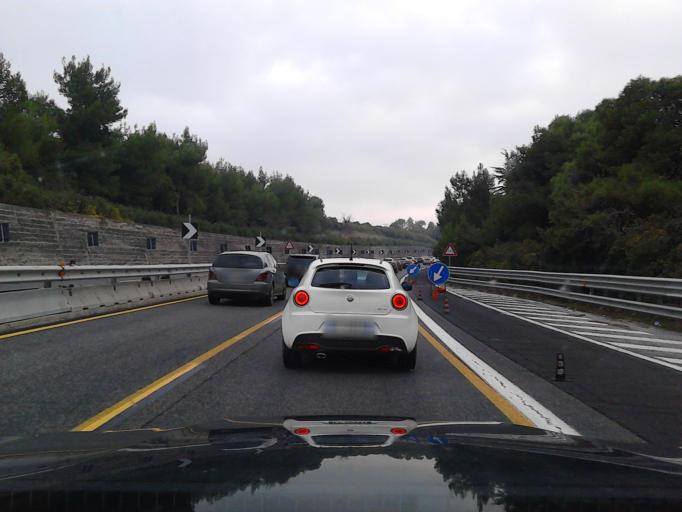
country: IT
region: Abruzzo
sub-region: Provincia di Teramo
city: Tortoreto Lido
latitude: 42.7875
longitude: 13.9351
